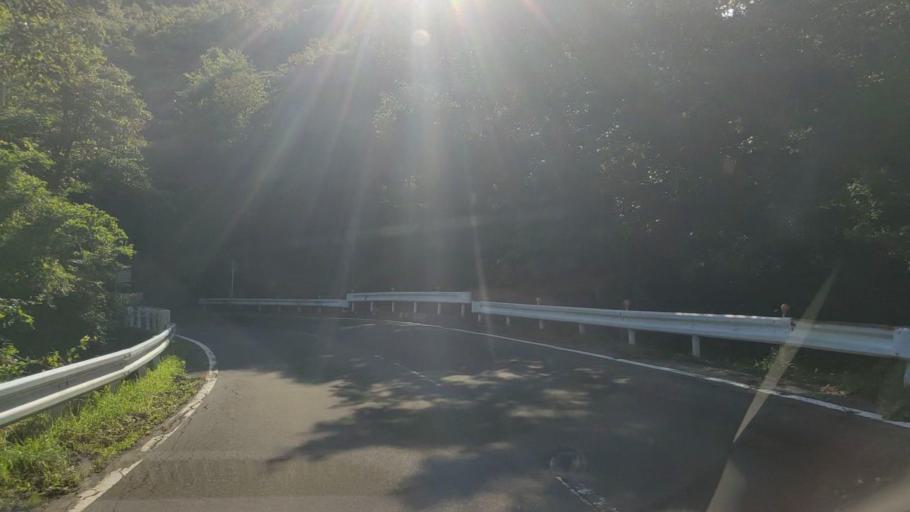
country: JP
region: Nagano
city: Suzaka
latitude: 36.5582
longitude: 138.5555
